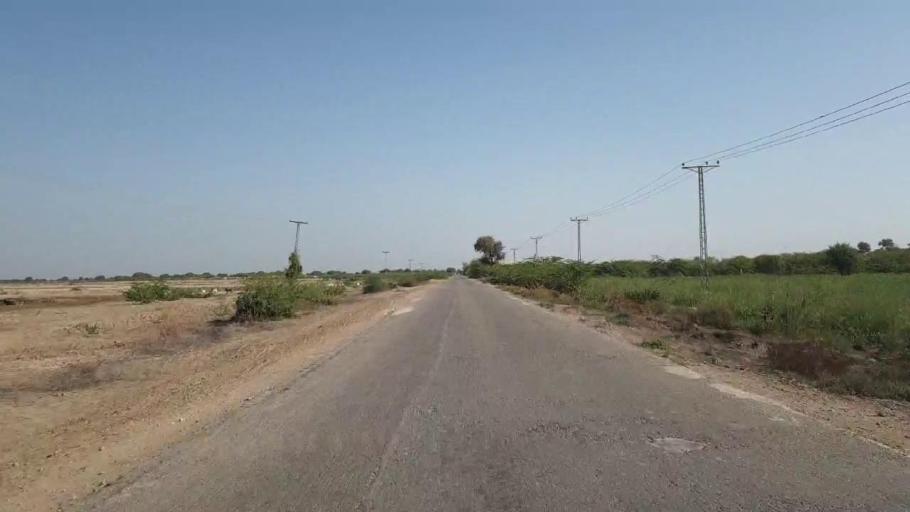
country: PK
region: Sindh
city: Umarkot
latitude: 25.4274
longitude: 69.7403
